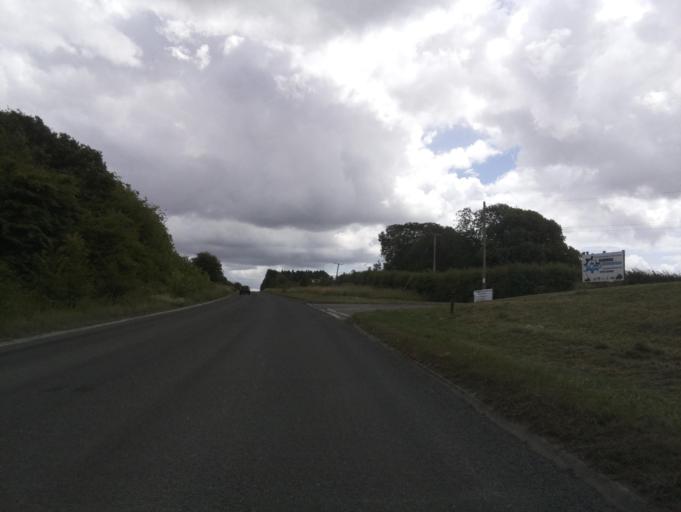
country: GB
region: England
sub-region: Wiltshire
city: Royal Wootton Bassett
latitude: 51.5583
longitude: -1.9075
